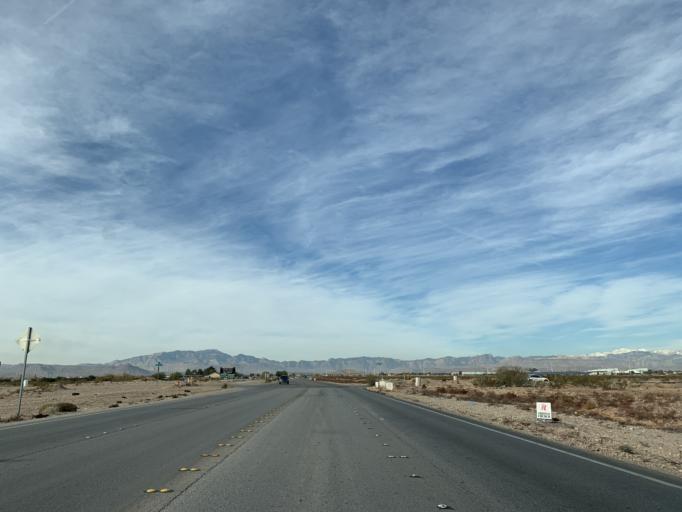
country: US
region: Nevada
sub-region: Clark County
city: Enterprise
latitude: 36.0136
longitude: -115.1889
